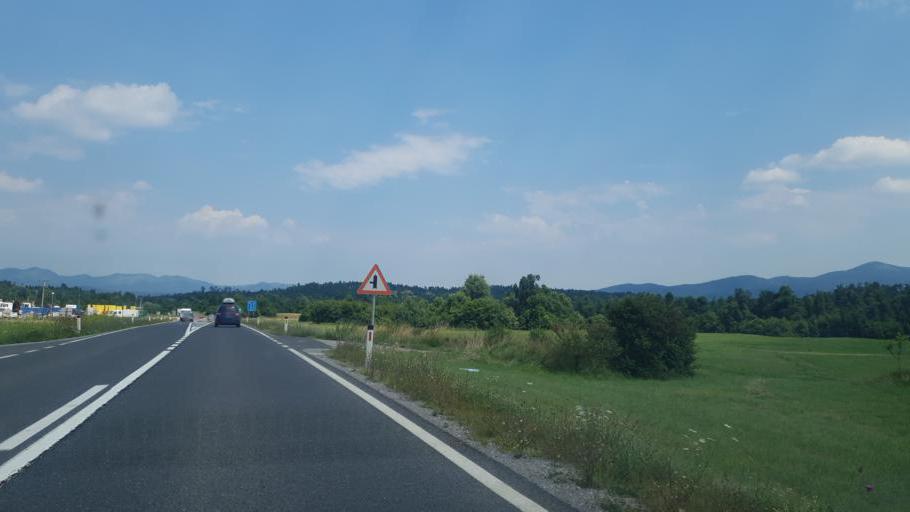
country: SI
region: Pivka
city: Pivka
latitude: 45.7182
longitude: 14.1914
